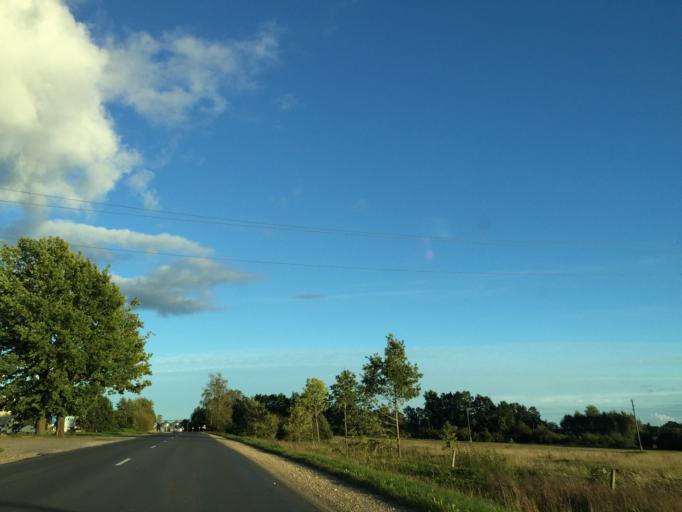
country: LV
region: Saldus Rajons
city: Saldus
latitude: 56.6913
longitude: 22.4493
